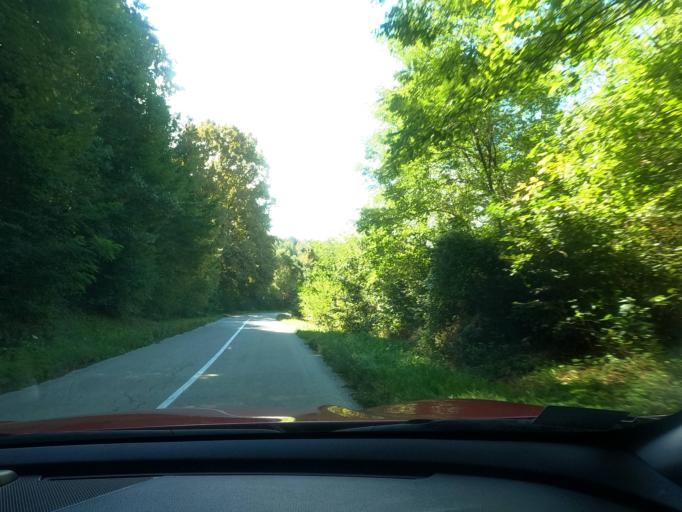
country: BA
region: Federation of Bosnia and Herzegovina
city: Vrnograc
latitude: 45.2343
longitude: 15.9287
